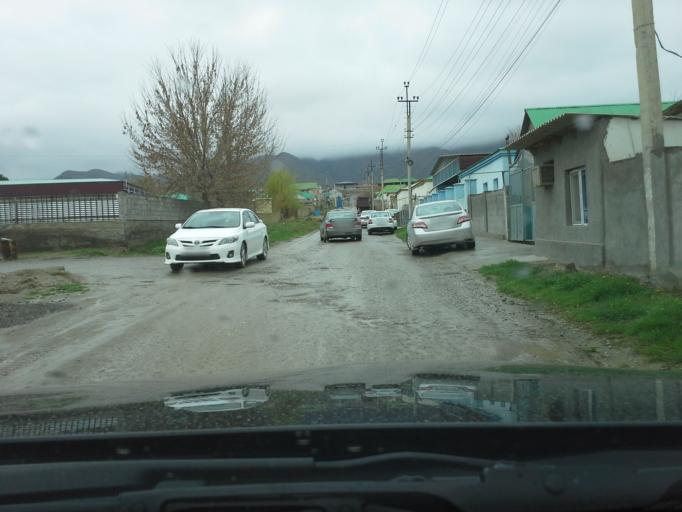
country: TM
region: Ahal
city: Abadan
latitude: 37.9631
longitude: 58.2066
